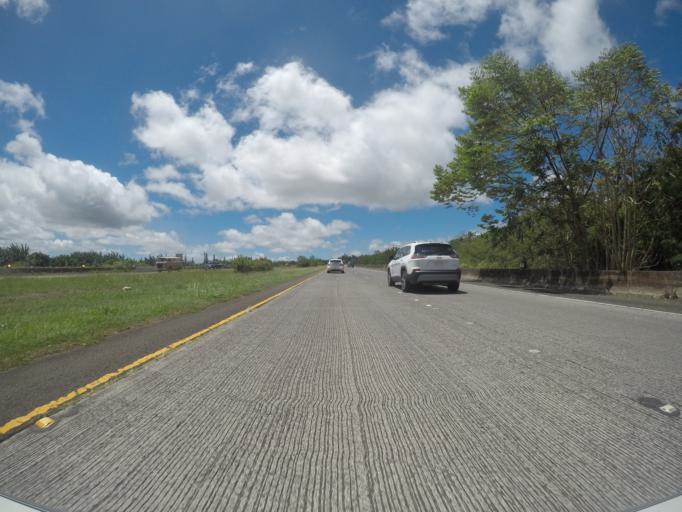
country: US
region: Hawaii
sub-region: Honolulu County
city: Wahiawa
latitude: 21.4841
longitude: -158.0251
